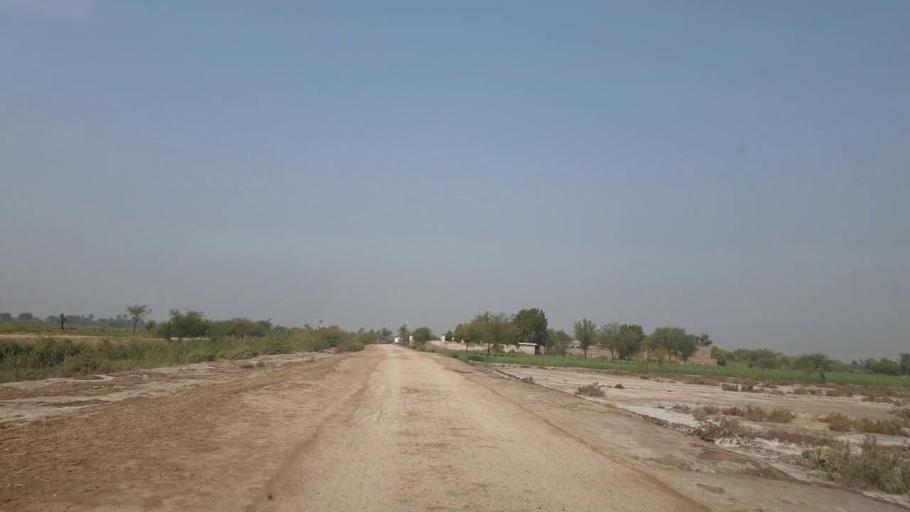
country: PK
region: Sindh
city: Mirpur Khas
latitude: 25.5510
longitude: 69.0767
